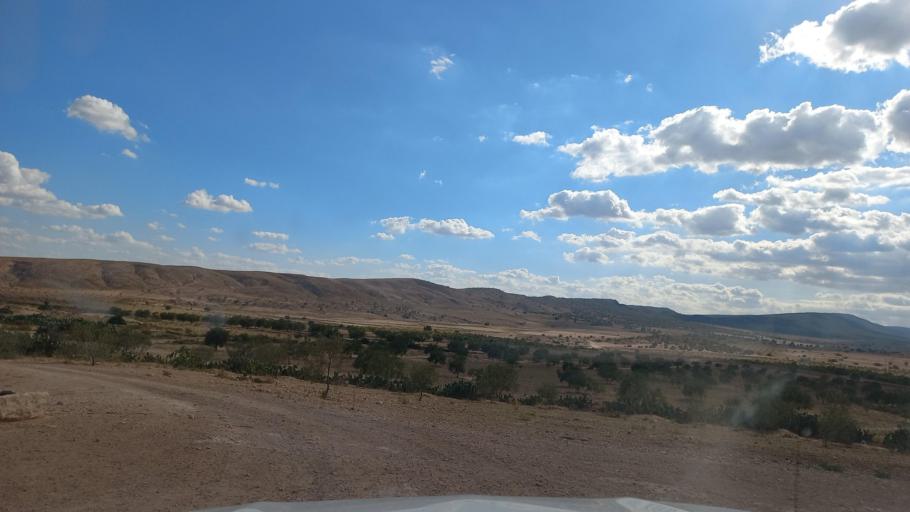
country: TN
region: Al Qasrayn
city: Sbiba
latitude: 35.4022
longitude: 9.0137
